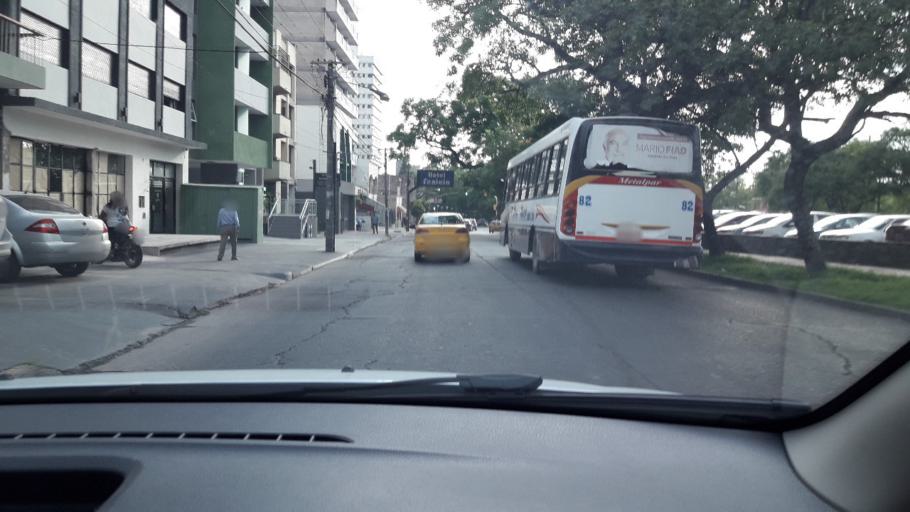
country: AR
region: Jujuy
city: San Salvador de Jujuy
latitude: -24.1886
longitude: -65.2999
